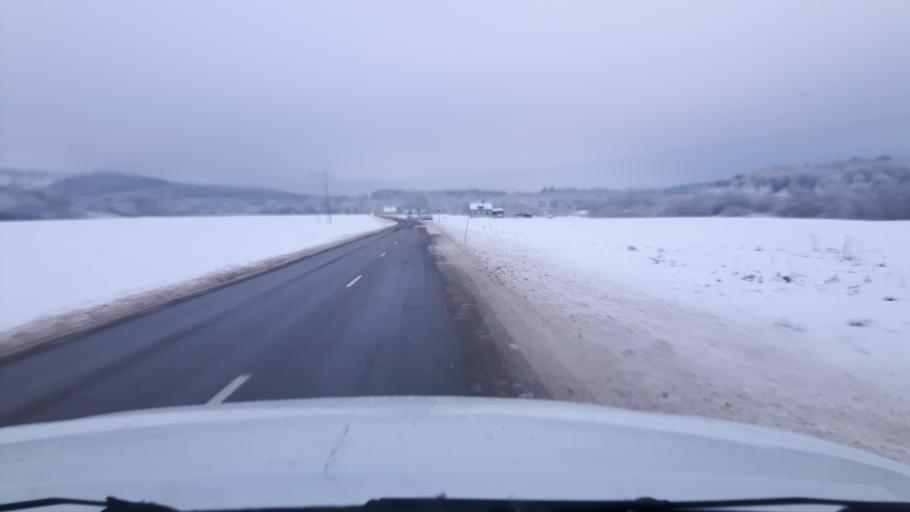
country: SE
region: Halland
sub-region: Kungsbacka Kommun
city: Fjaeras kyrkby
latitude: 57.4233
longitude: 12.1986
